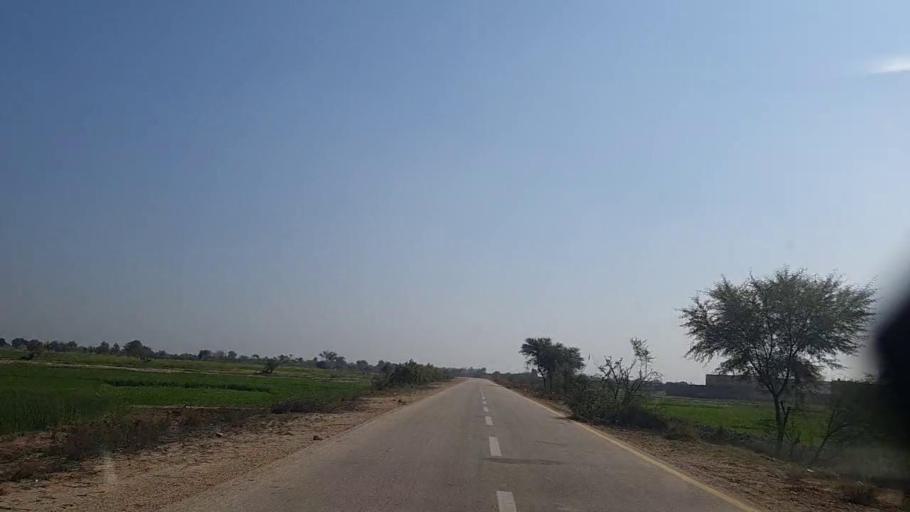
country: PK
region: Sindh
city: Nawabshah
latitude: 26.2062
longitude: 68.3625
